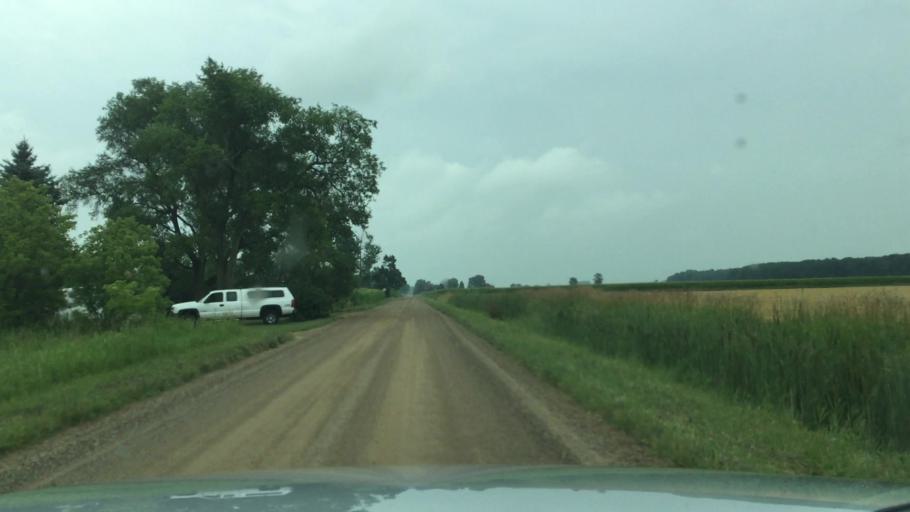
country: US
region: Michigan
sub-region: Shiawassee County
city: New Haven
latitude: 43.1155
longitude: -84.2291
